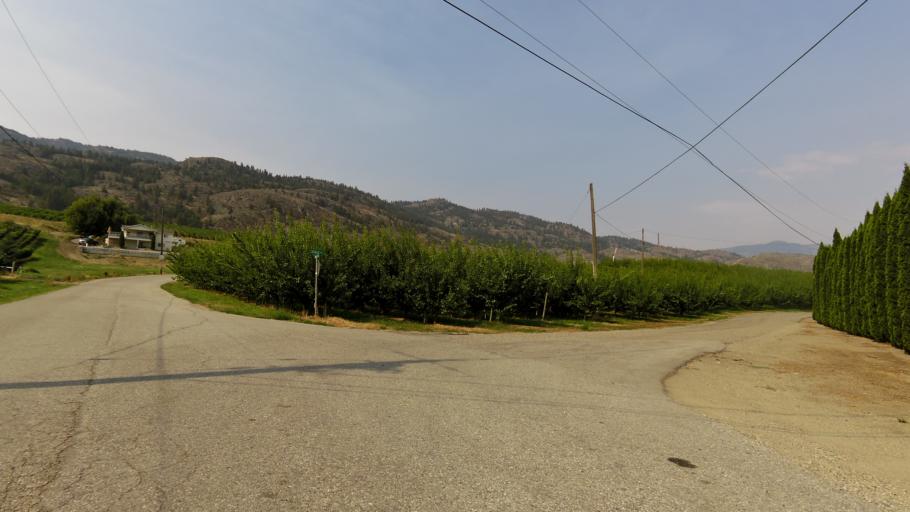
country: CA
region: British Columbia
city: Osoyoos
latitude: 49.0529
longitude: -119.5068
